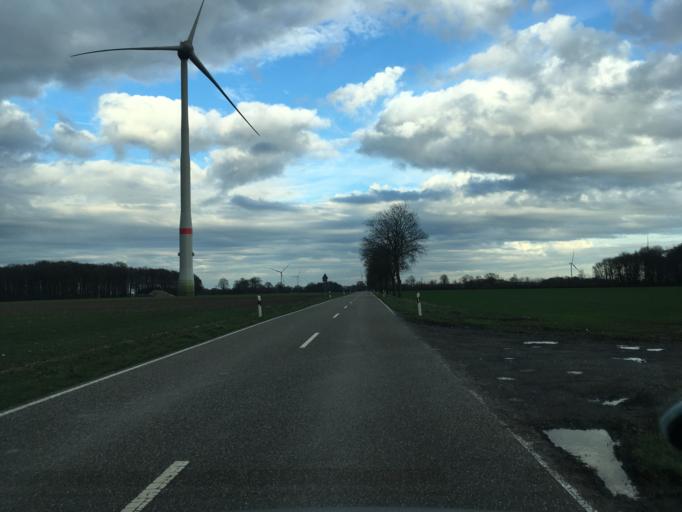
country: DE
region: North Rhine-Westphalia
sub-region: Regierungsbezirk Munster
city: Schoppingen
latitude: 52.0614
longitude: 7.1741
